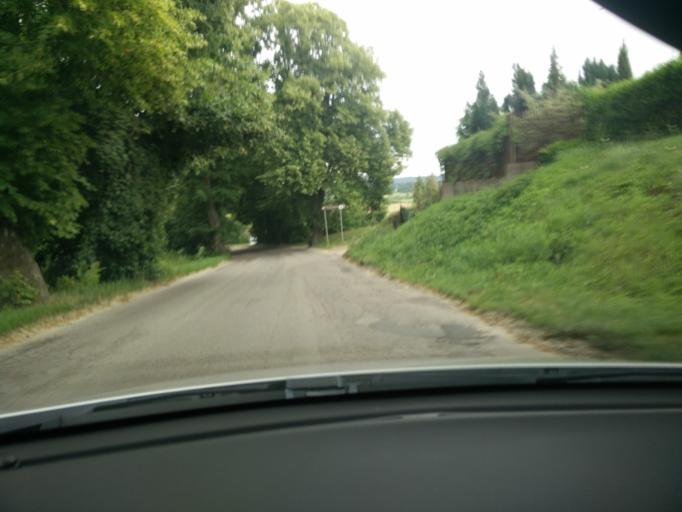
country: PL
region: Pomeranian Voivodeship
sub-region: Powiat pucki
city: Mrzezino
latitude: 54.6500
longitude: 18.4326
